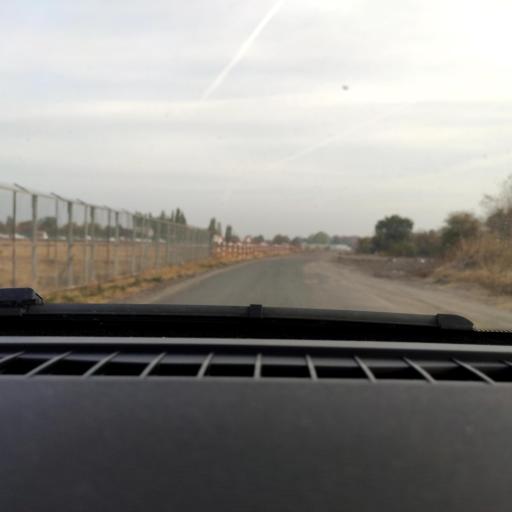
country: RU
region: Voronezj
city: Voronezh
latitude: 51.6613
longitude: 39.2686
